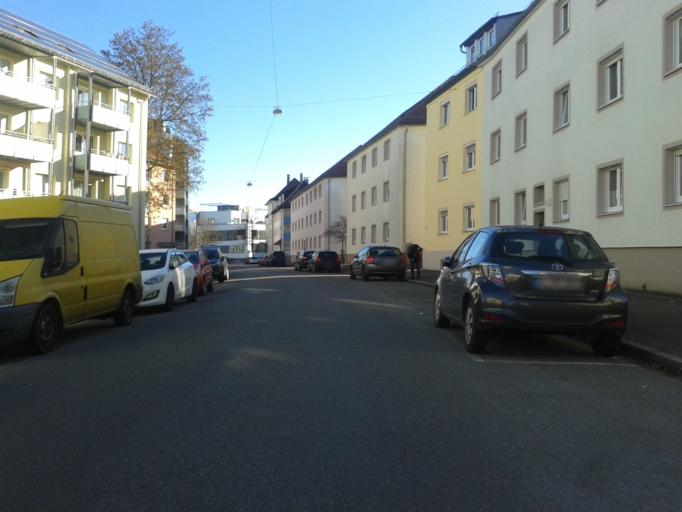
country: DE
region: Baden-Wuerttemberg
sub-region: Tuebingen Region
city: Ulm
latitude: 48.3921
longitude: 9.9618
